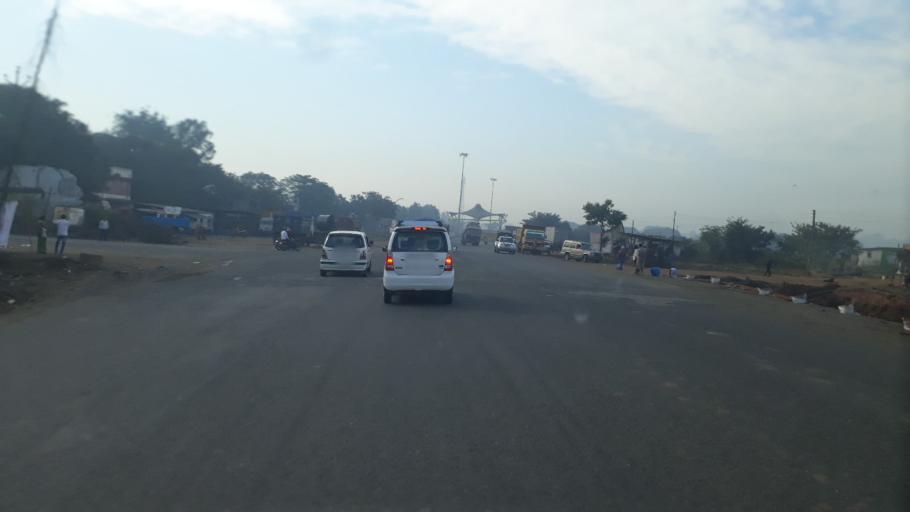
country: IN
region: Maharashtra
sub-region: Raigarh
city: Pen
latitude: 18.8477
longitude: 73.0951
